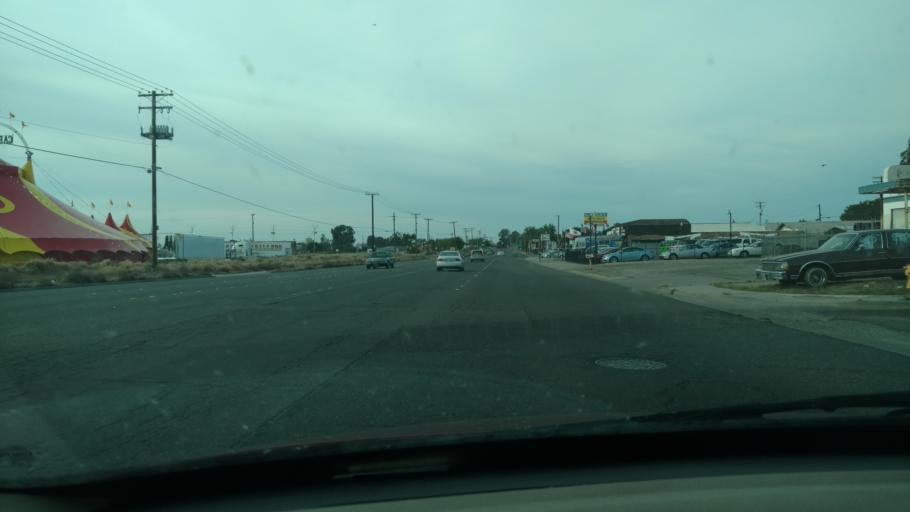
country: US
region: California
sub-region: Stanislaus County
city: Shackelford
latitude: 37.6139
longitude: -120.9936
